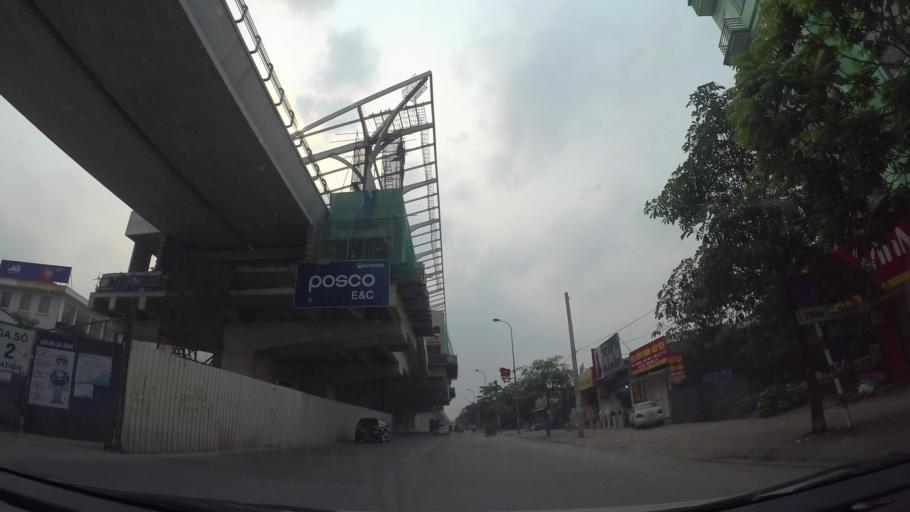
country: VN
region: Ha Noi
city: Cau Dien
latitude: 21.0478
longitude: 105.7455
